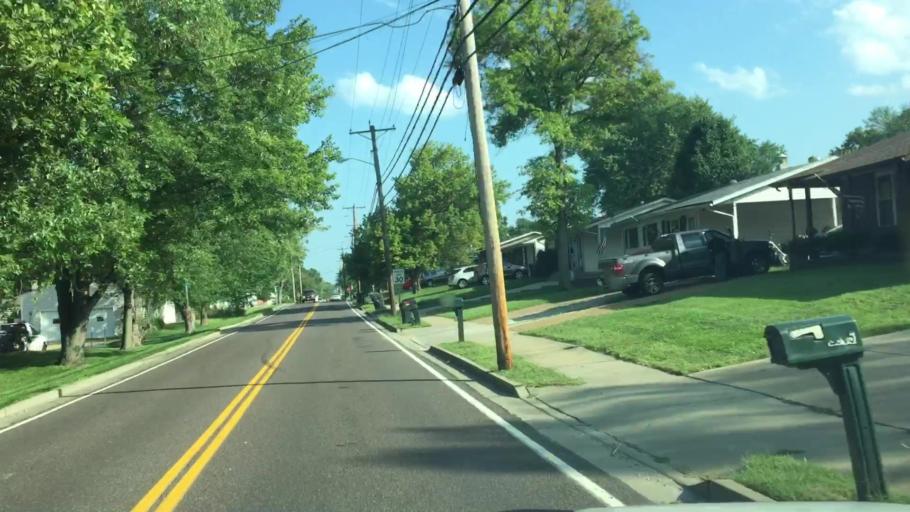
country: US
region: Missouri
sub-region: Jefferson County
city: Arnold
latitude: 38.4480
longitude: -90.3569
